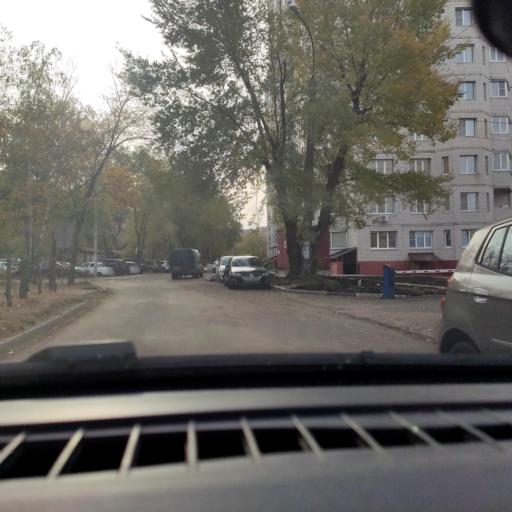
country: RU
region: Voronezj
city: Voronezh
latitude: 51.7158
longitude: 39.2698
